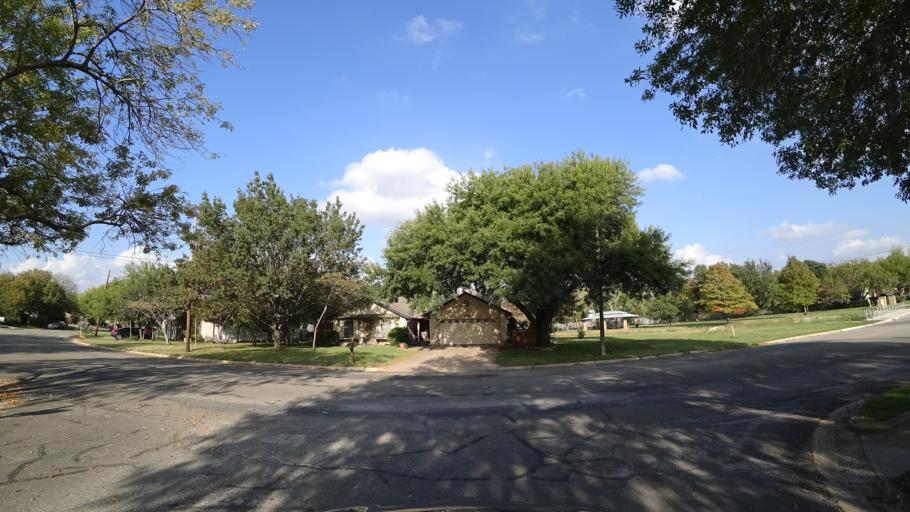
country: US
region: Texas
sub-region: Williamson County
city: Round Rock
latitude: 30.4930
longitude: -97.6676
